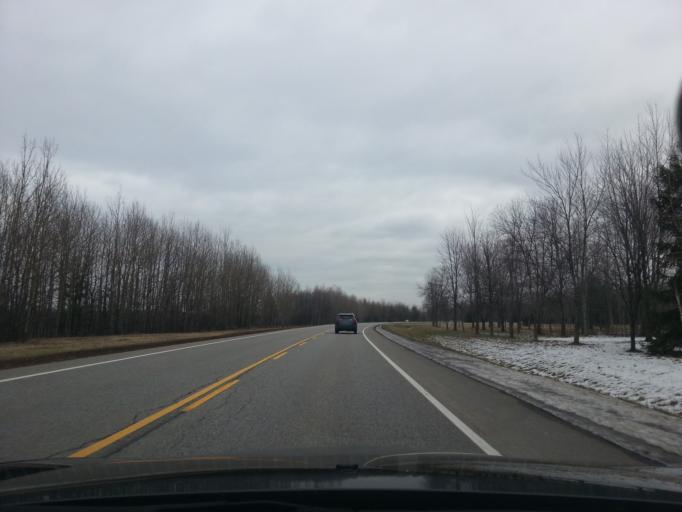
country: CA
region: Quebec
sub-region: Outaouais
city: Gatineau
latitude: 45.4642
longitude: -75.6019
